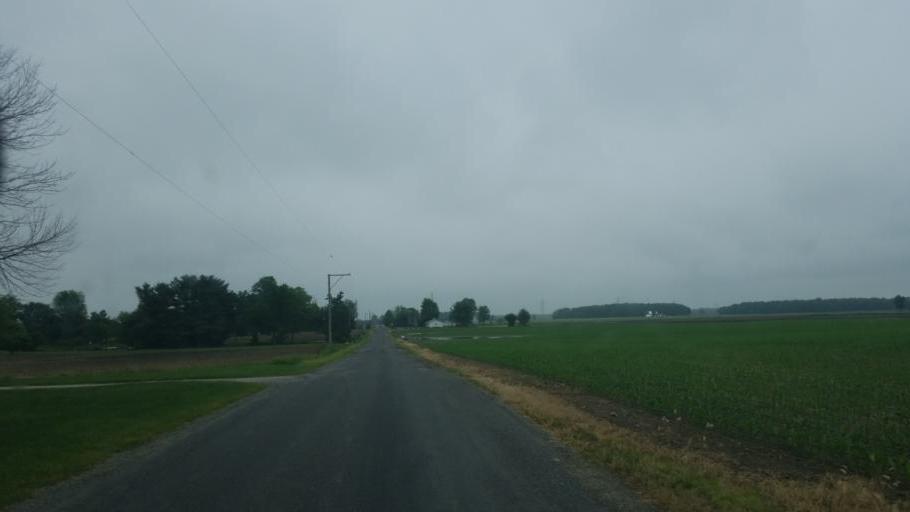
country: US
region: Indiana
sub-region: Marshall County
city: Bremen
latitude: 41.4793
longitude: -86.1415
